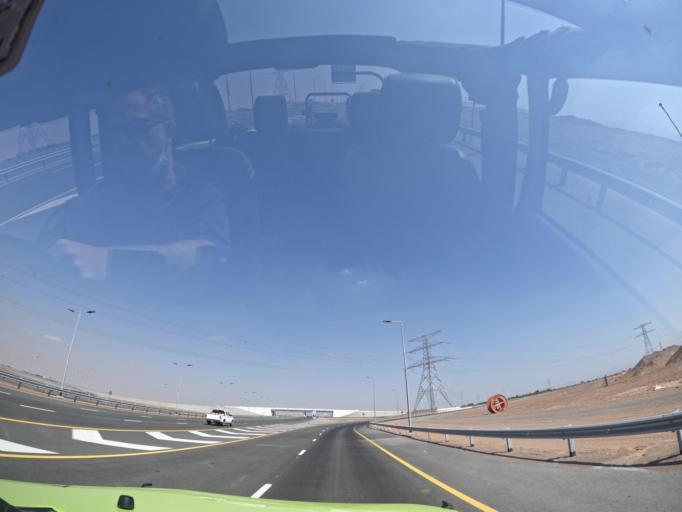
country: AE
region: Ash Shariqah
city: Adh Dhayd
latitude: 24.8106
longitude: 55.8020
